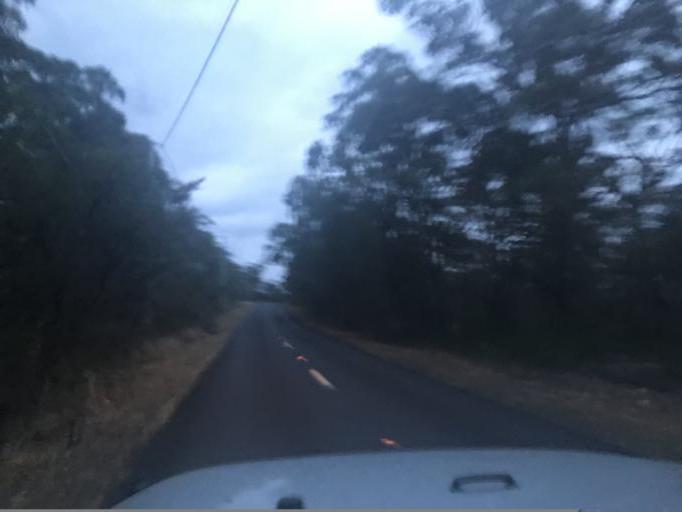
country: AU
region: New South Wales
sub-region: Hawkesbury
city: Pitt Town
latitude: -33.4690
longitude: 150.8532
